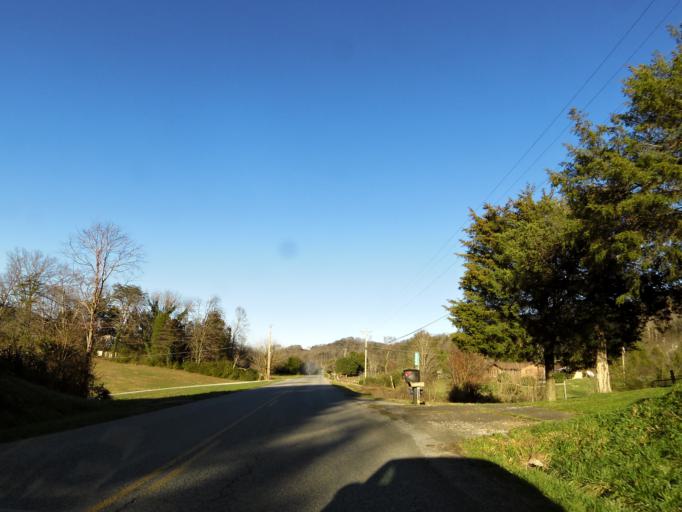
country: US
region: Tennessee
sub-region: Anderson County
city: Clinton
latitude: 36.1521
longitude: -84.1745
